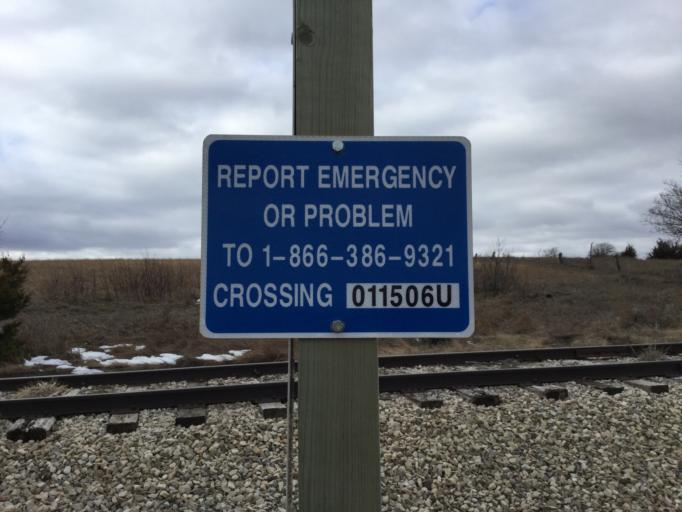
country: US
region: Kansas
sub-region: Lincoln County
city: Lincoln
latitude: 39.1938
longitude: -98.3775
